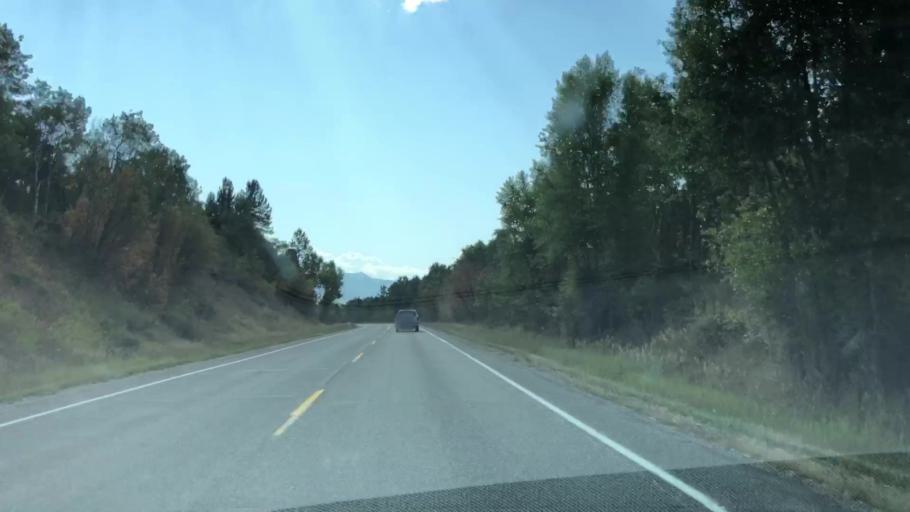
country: US
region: Wyoming
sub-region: Teton County
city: Hoback
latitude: 43.2111
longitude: -111.0593
